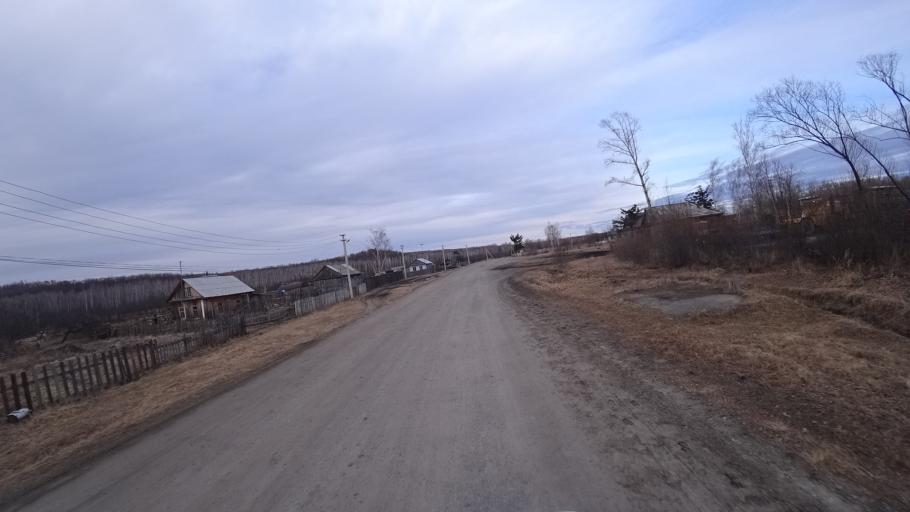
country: RU
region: Amur
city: Bureya
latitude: 50.0206
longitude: 129.7754
